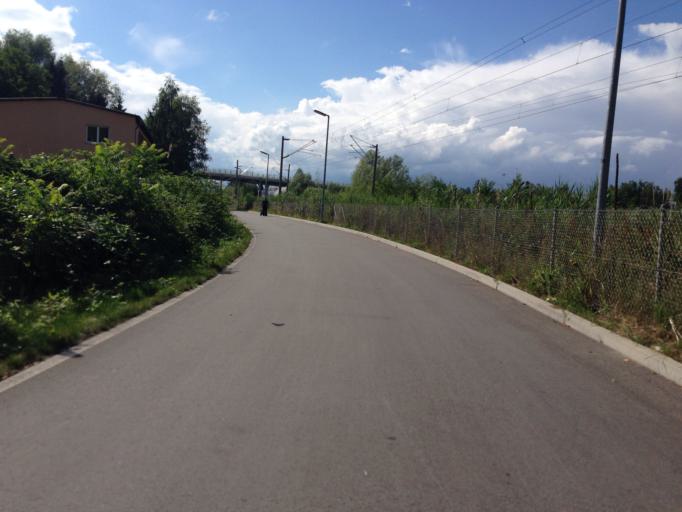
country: CH
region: Thurgau
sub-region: Kreuzlingen District
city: Gottlieben
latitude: 47.6863
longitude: 9.1349
